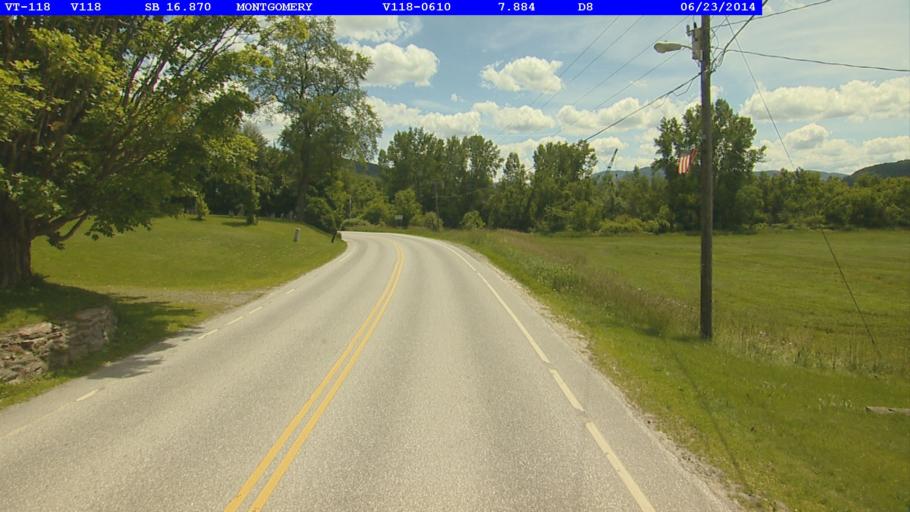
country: US
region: Vermont
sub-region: Franklin County
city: Richford
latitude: 44.9006
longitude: -72.6374
